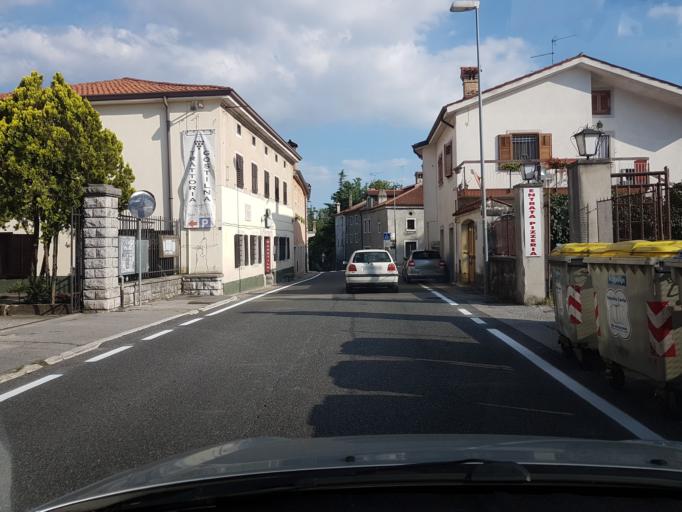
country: IT
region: Friuli Venezia Giulia
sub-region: Provincia di Trieste
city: Prosecco-Contovello
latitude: 45.7038
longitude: 13.7330
